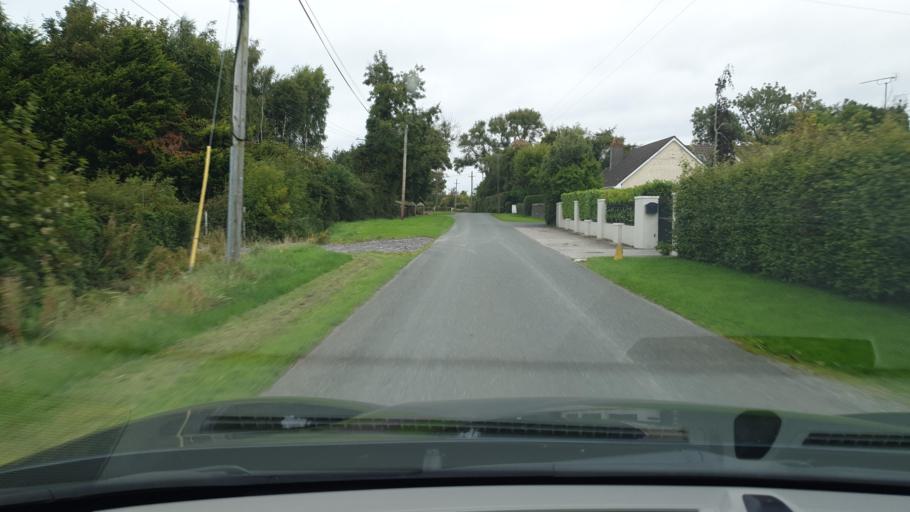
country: IE
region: Leinster
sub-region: An Mhi
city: Ratoath
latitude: 53.4978
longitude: -6.4894
